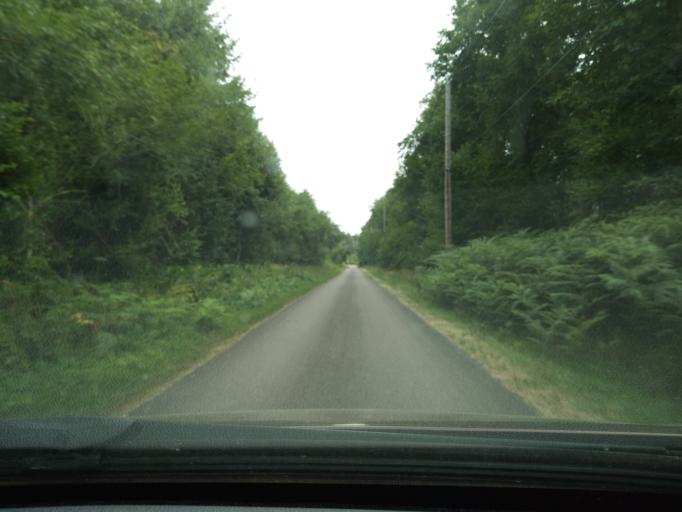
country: FR
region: Bourgogne
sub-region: Departement de la Cote-d'Or
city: Saulieu
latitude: 47.3516
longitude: 4.0929
